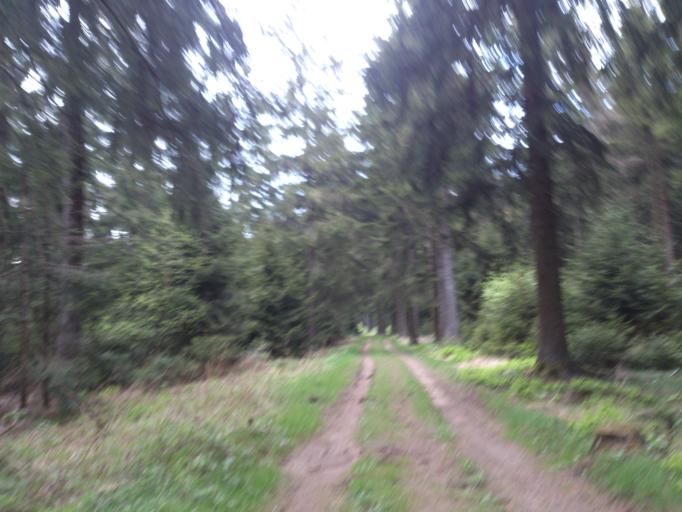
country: DE
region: North Rhine-Westphalia
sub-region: Regierungsbezirk Detmold
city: Willebadessen
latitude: 51.5944
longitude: 9.0140
